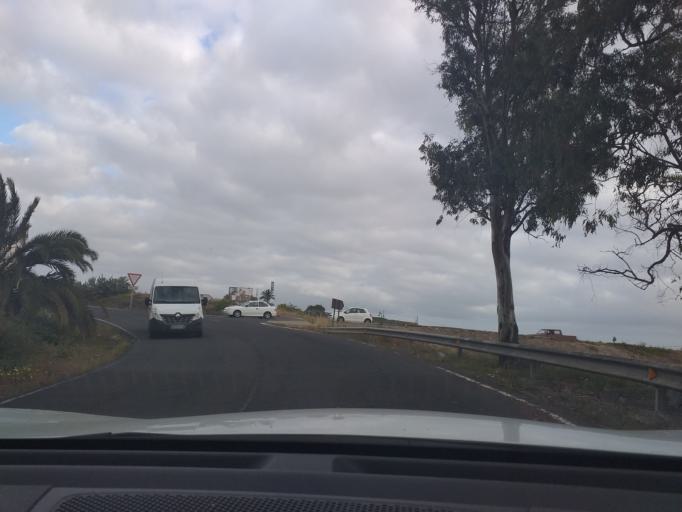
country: ES
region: Canary Islands
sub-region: Provincia de Las Palmas
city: Arucas
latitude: 28.1040
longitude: -15.4865
